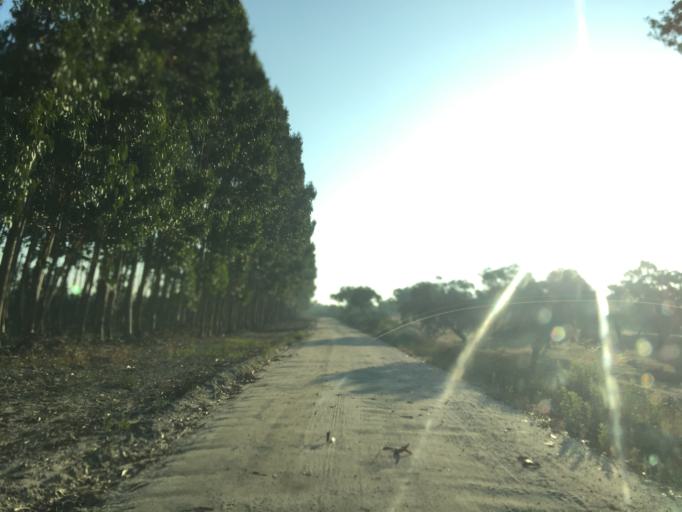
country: PT
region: Portalegre
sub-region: Ponte de Sor
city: Santo Andre
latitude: 39.1125
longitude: -8.3362
